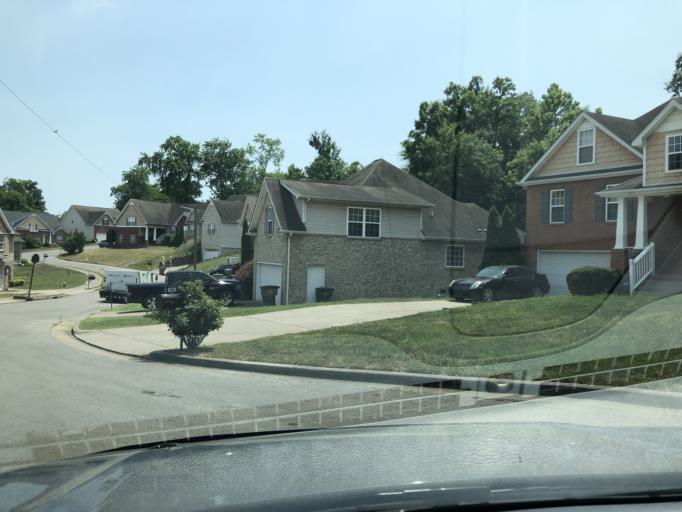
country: US
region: Tennessee
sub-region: Rutherford County
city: La Vergne
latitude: 36.0475
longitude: -86.6221
